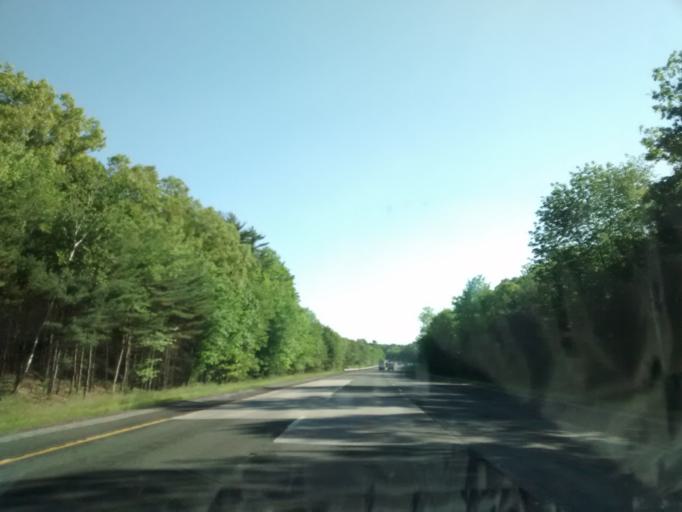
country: US
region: Massachusetts
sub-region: Hampden County
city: Holland
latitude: 42.0572
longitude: -72.1160
